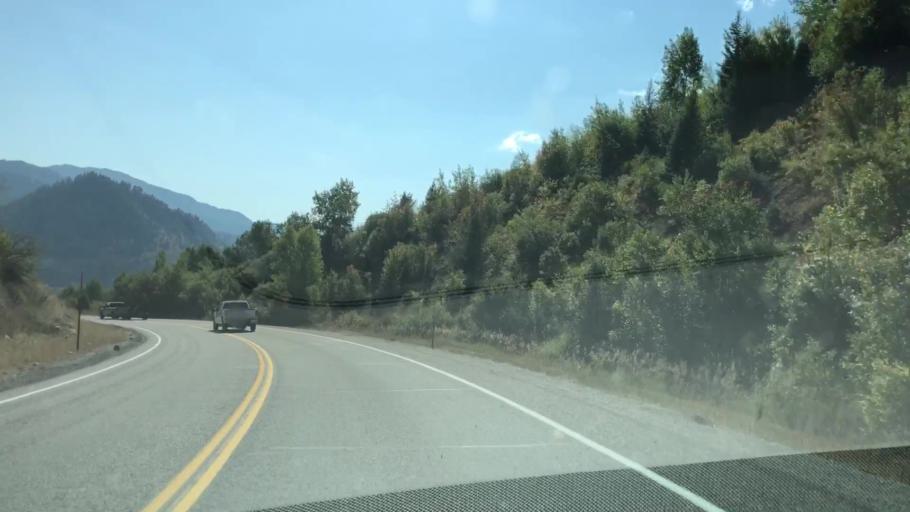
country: US
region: Idaho
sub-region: Teton County
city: Victor
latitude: 43.3191
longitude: -111.1651
